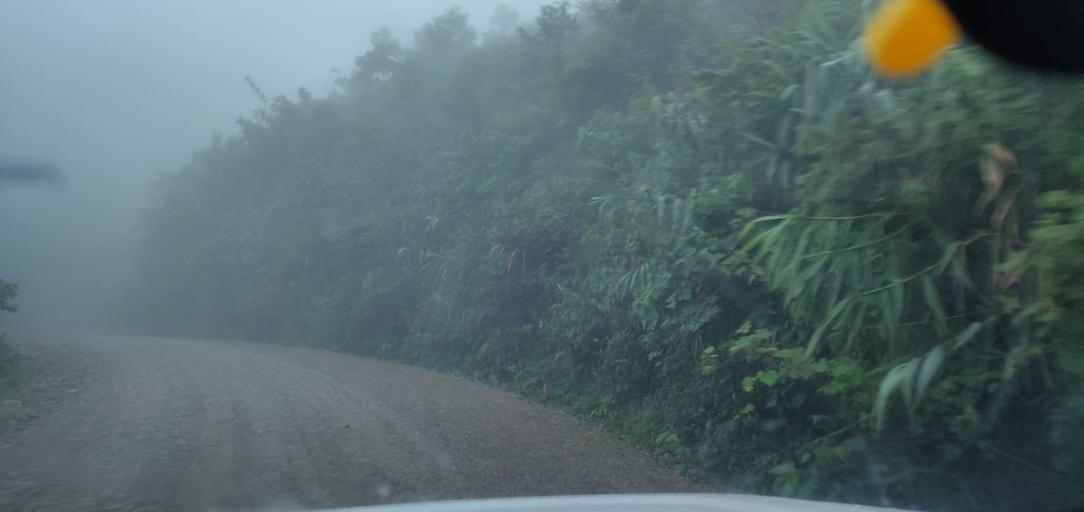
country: LA
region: Phongsali
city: Phongsali
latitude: 21.3924
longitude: 102.1920
